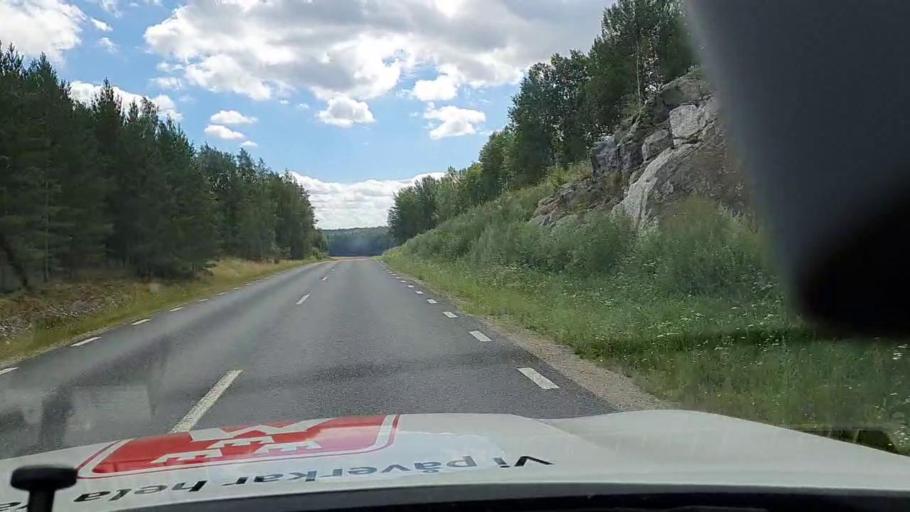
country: SE
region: Soedermanland
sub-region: Nykopings Kommun
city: Olstorp
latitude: 58.7534
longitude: 16.6162
